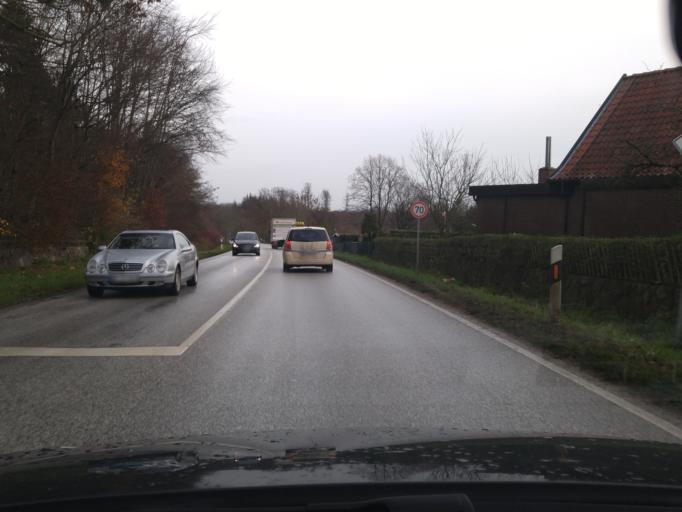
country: DE
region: Schleswig-Holstein
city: Timmendorfer Strand
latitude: 53.9933
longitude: 10.7696
